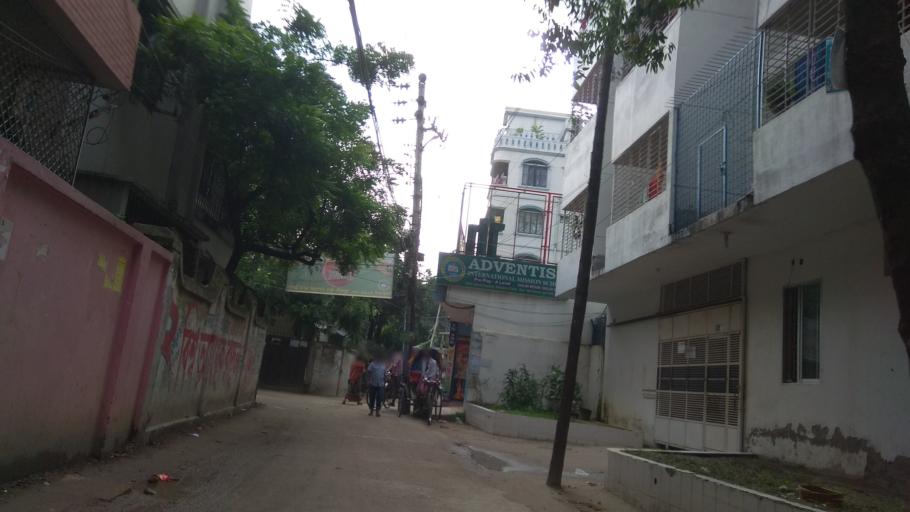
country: BD
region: Dhaka
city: Azimpur
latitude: 23.7934
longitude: 90.3802
